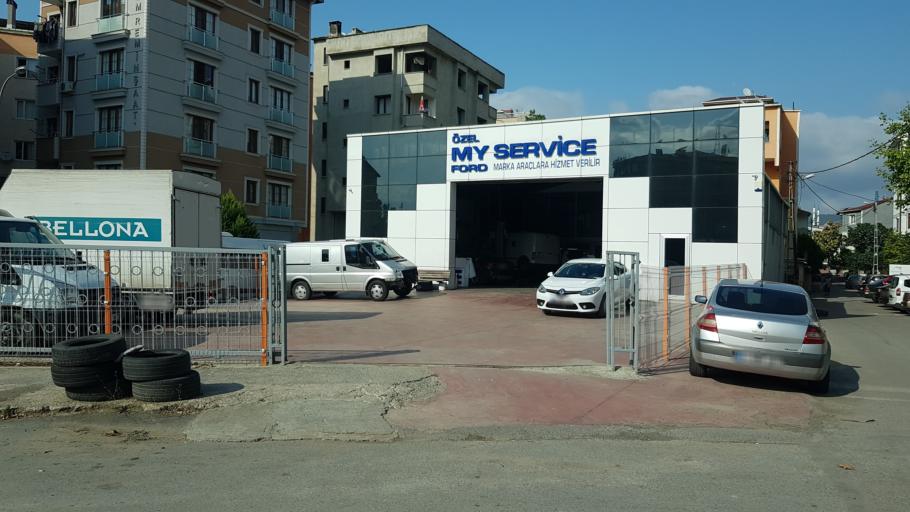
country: TR
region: Istanbul
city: Maltepe
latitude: 40.9067
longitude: 29.1922
